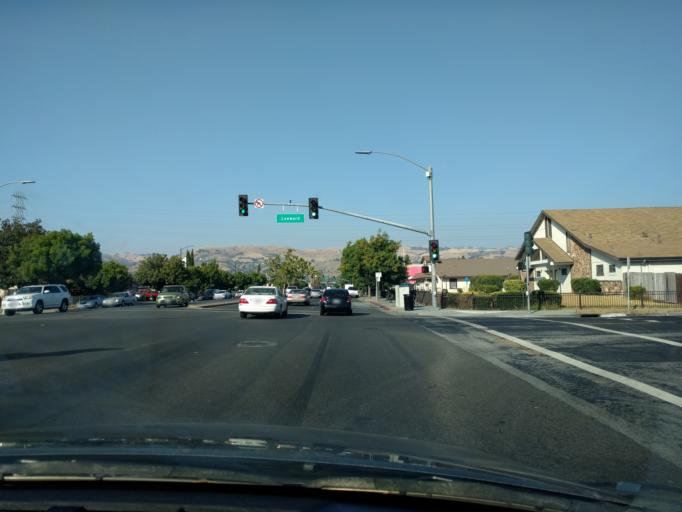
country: US
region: California
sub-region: Santa Clara County
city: Alum Rock
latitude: 37.3482
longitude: -121.8307
